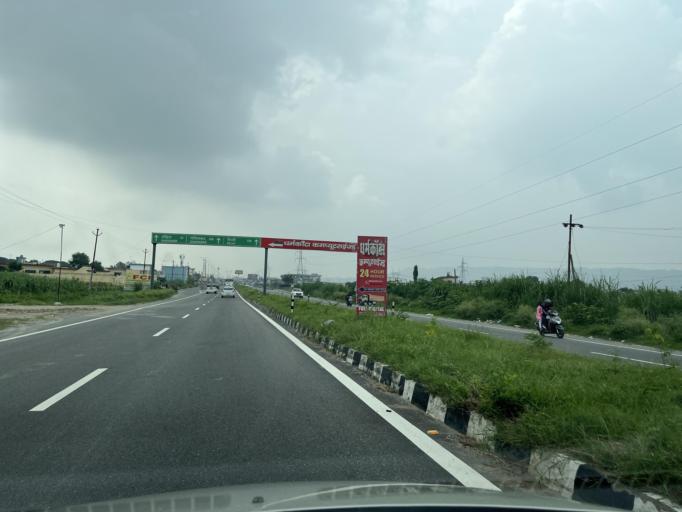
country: IN
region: Uttarakhand
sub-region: Dehradun
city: Raiwala
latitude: 30.0846
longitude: 78.1890
